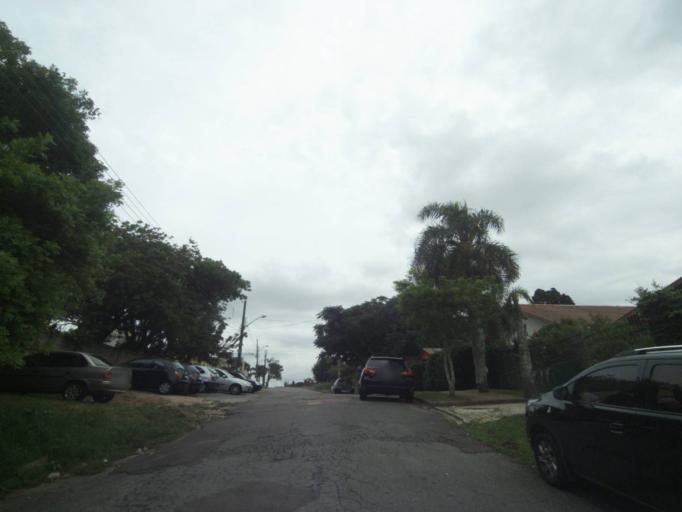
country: BR
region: Parana
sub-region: Curitiba
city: Curitiba
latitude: -25.4018
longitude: -49.2893
